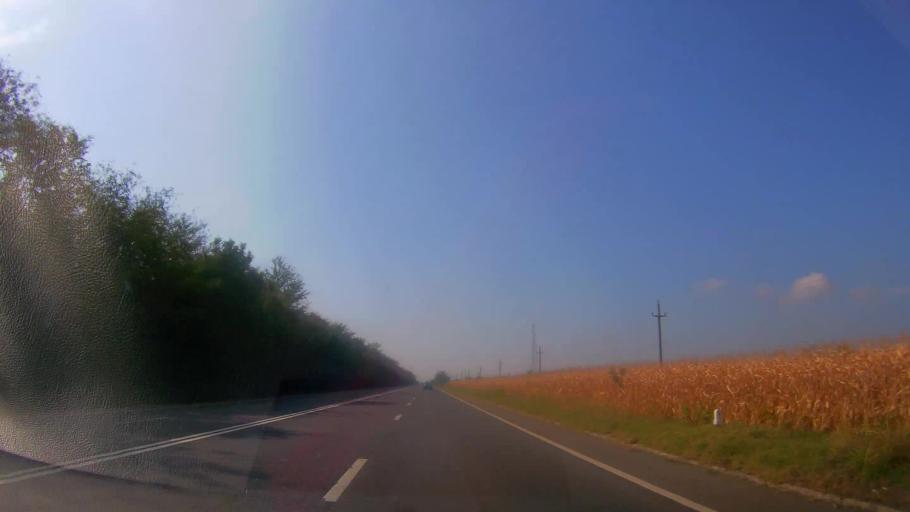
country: RO
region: Giurgiu
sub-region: Comuna Daia
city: Plopsoru
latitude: 44.0442
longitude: 25.9769
